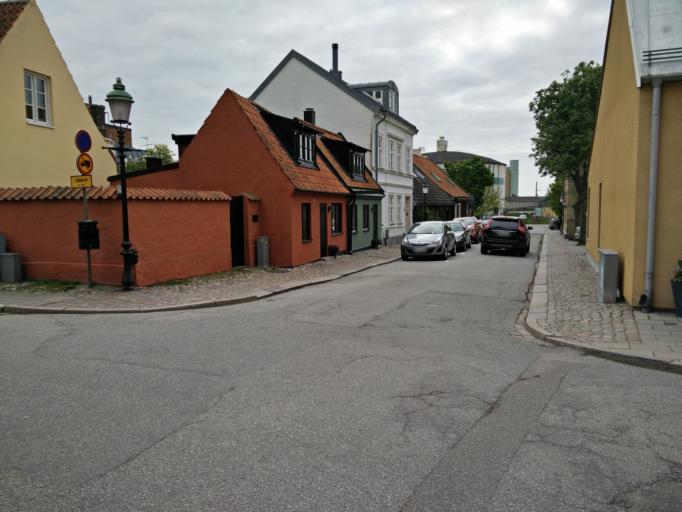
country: SE
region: Skane
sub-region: Ystads Kommun
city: Ystad
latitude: 55.4286
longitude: 13.8191
